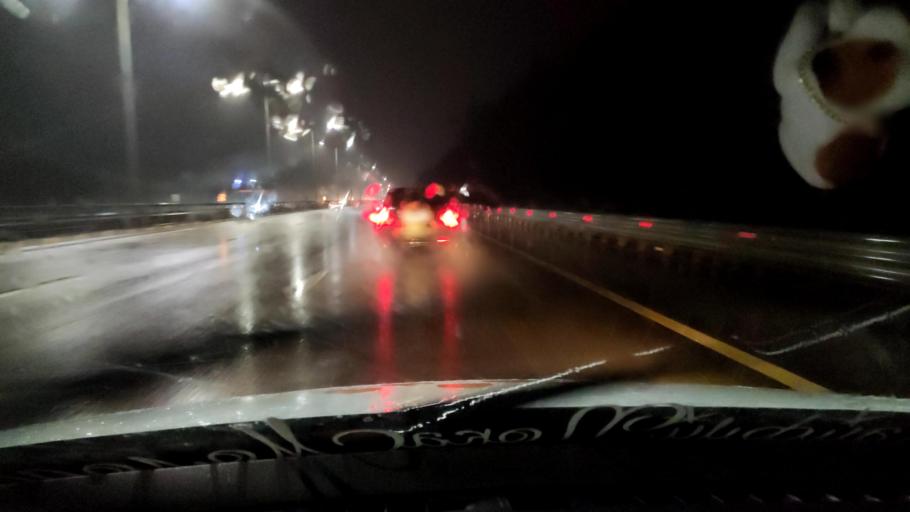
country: RU
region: Voronezj
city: Somovo
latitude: 51.7017
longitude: 39.3050
